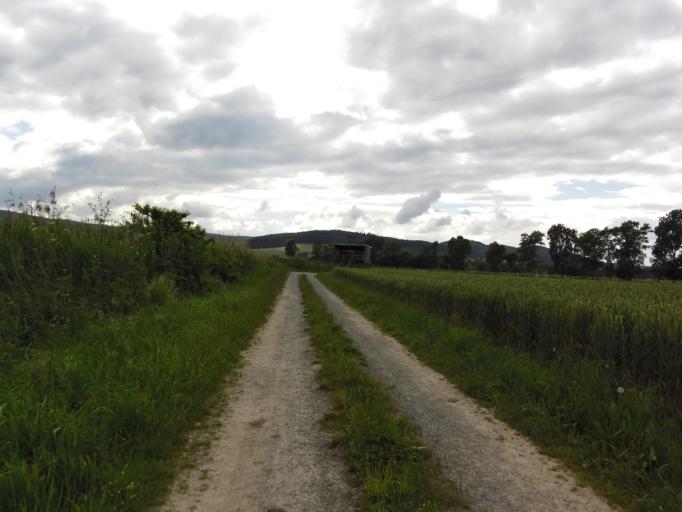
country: DE
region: Thuringia
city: Creuzburg
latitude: 51.0440
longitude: 10.2333
